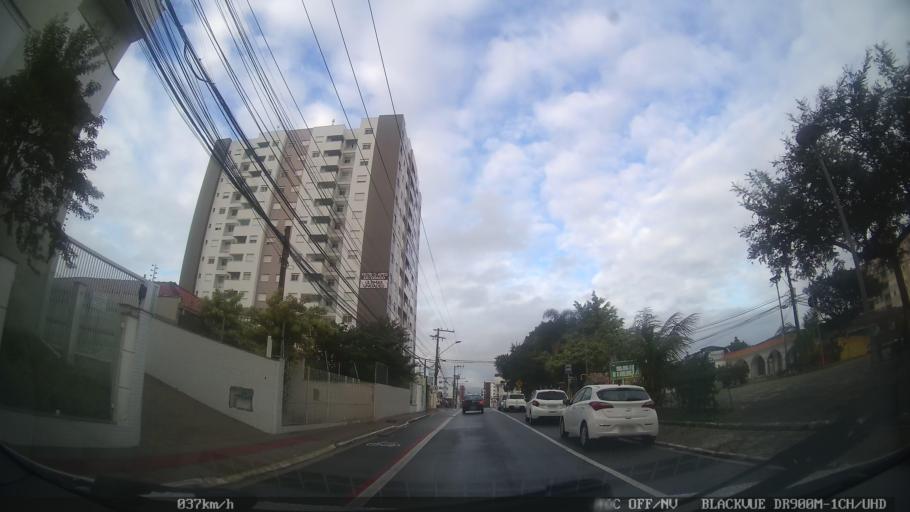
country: BR
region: Santa Catarina
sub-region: Sao Jose
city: Campinas
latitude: -27.5792
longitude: -48.6079
